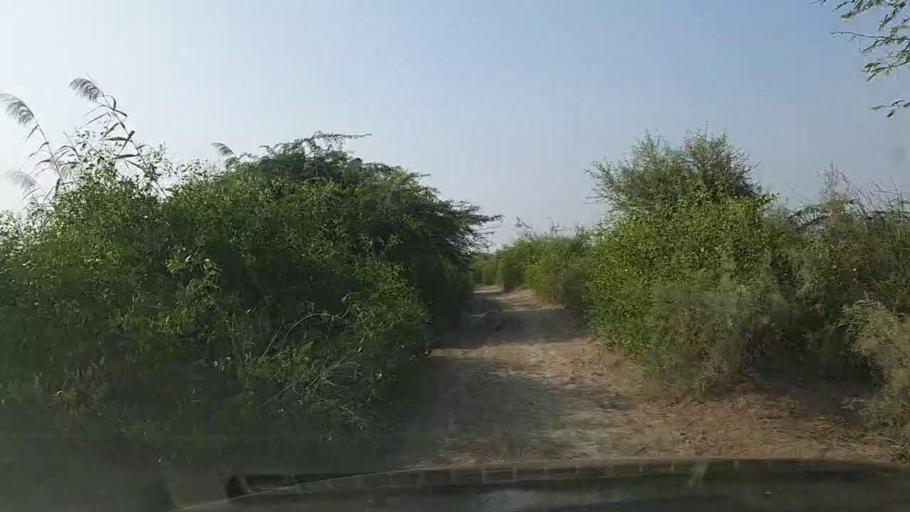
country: PK
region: Sindh
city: Mirpur Batoro
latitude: 24.6477
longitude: 68.2785
